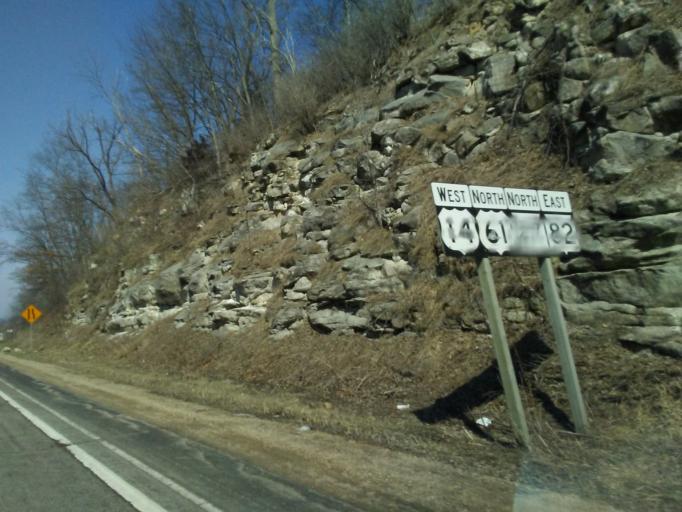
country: US
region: Wisconsin
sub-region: Vernon County
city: Viroqua
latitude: 43.5228
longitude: -90.8659
